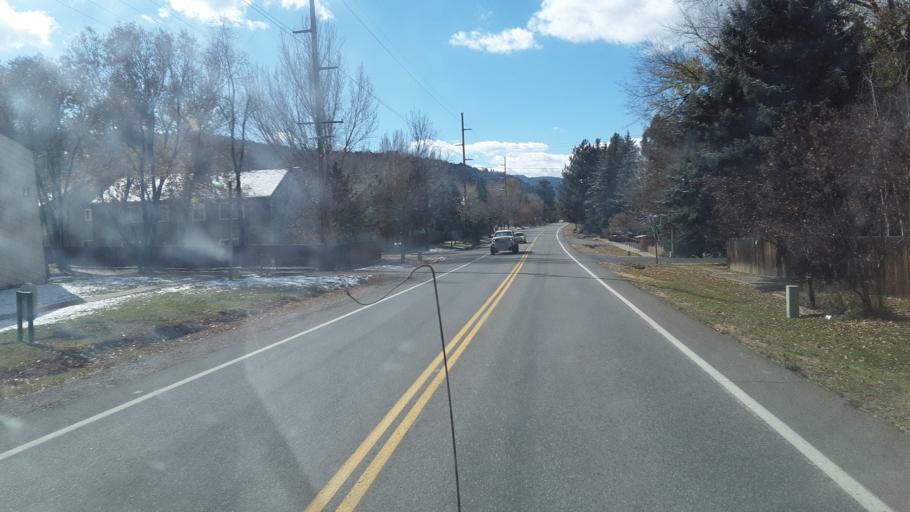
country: US
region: Colorado
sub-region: La Plata County
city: Durango
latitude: 37.3024
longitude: -107.8382
